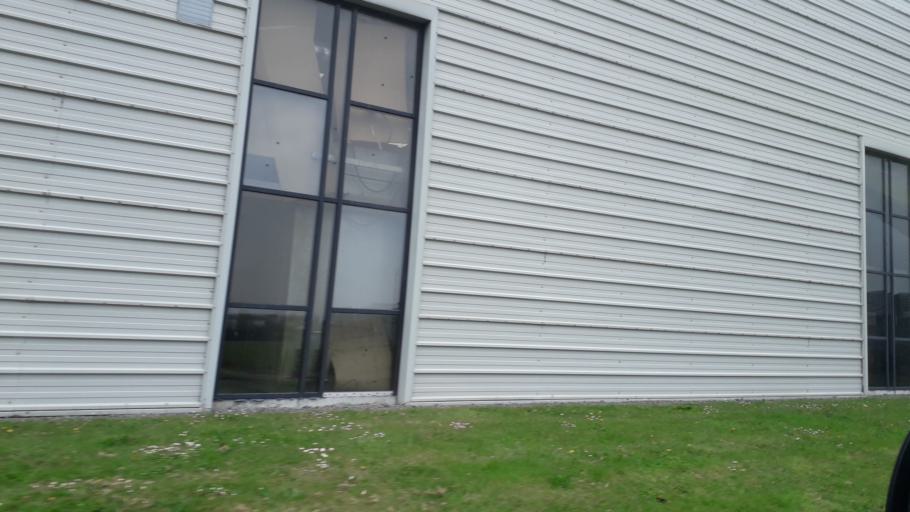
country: IE
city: Bonnybrook
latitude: 53.4024
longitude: -6.2231
